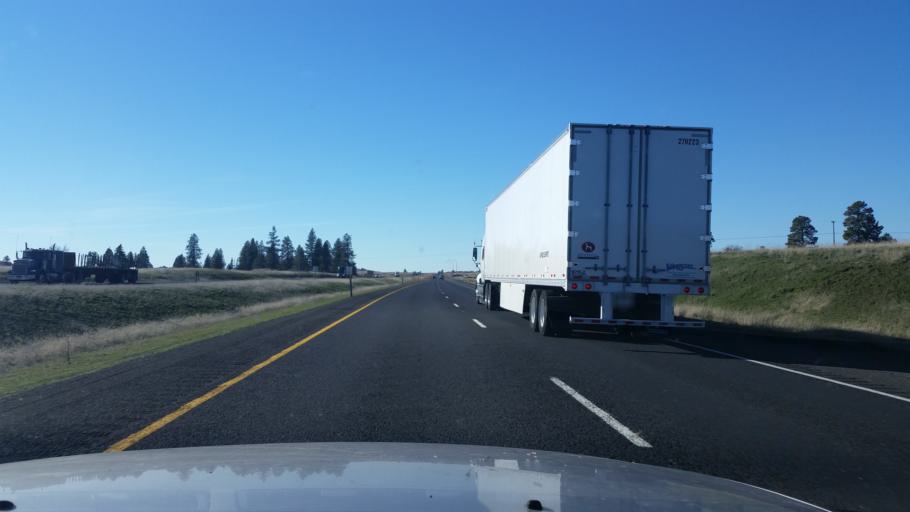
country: US
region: Washington
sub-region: Spokane County
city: Medical Lake
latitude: 47.3957
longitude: -117.8414
